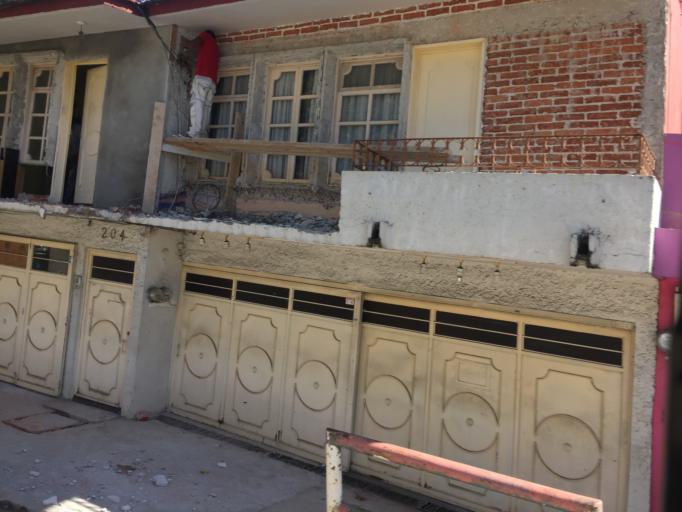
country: MX
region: Veracruz
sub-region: Xalapa
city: Xalapa de Enriquez
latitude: 19.5346
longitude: -96.8910
